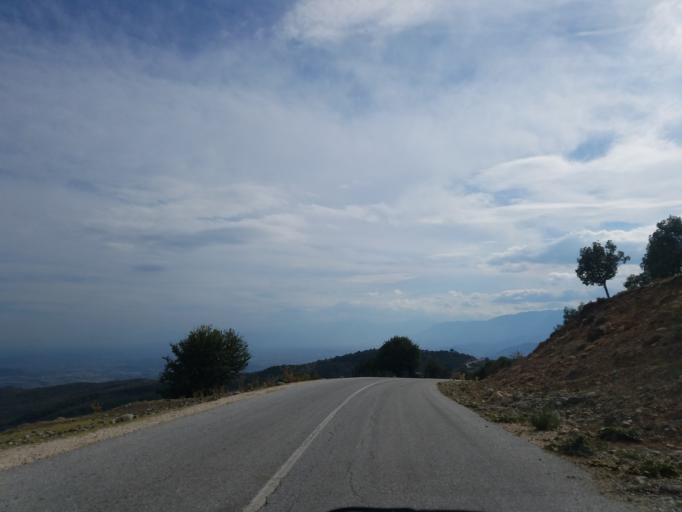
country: GR
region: Thessaly
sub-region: Trikala
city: Kastraki
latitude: 39.7636
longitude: 21.6647
